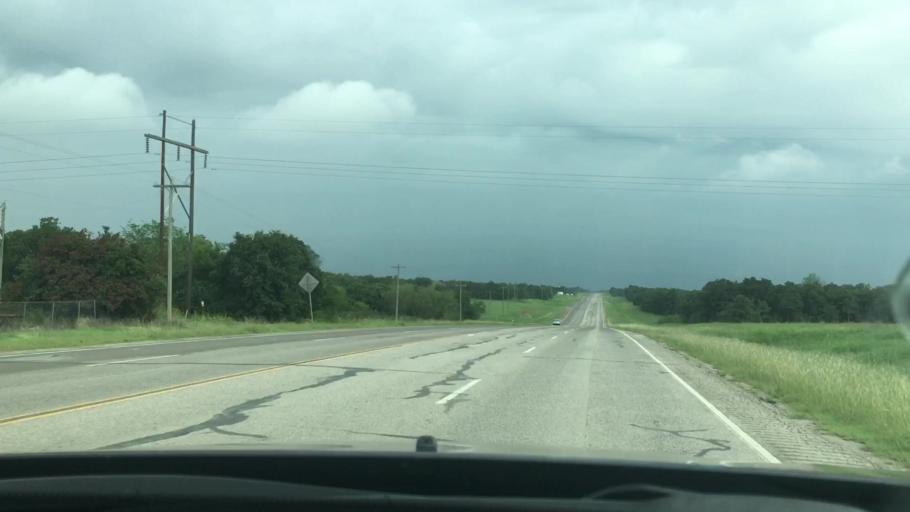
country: US
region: Oklahoma
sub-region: Carter County
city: Wilson
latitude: 34.1796
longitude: -97.4747
